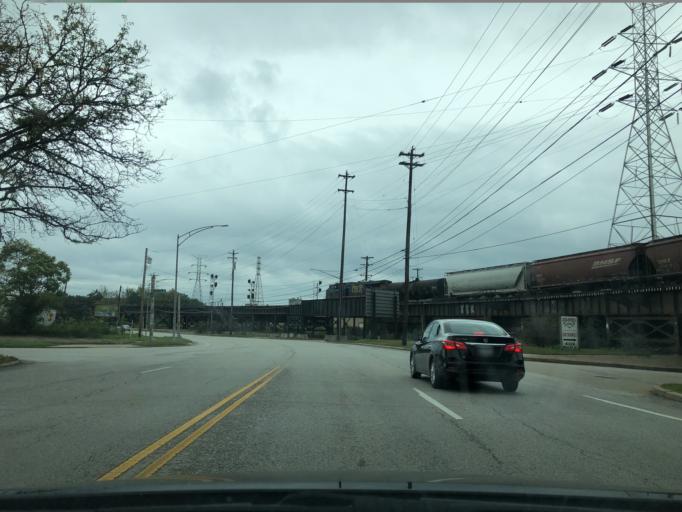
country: US
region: Kentucky
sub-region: Kenton County
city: Ludlow
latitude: 39.0989
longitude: -84.5299
